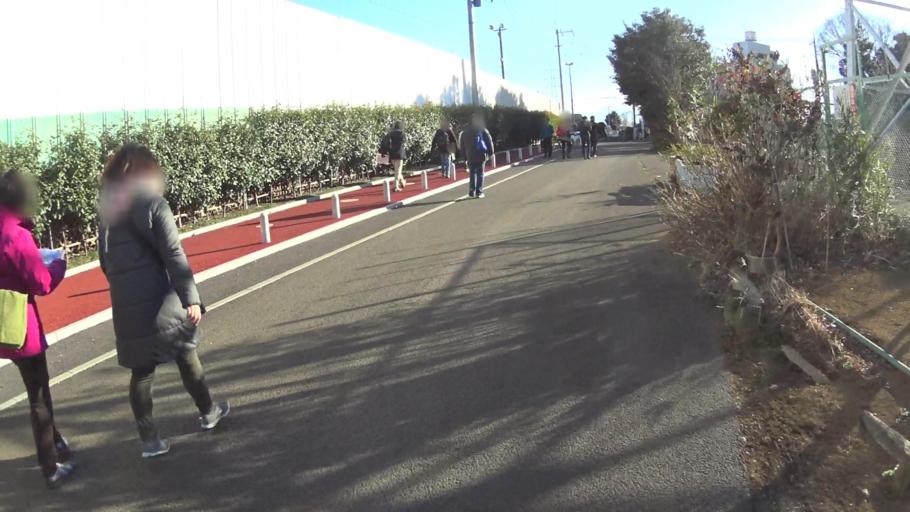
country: JP
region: Saitama
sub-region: Kawaguchi-shi
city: Hatogaya-honcho
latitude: 35.8905
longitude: 139.7183
